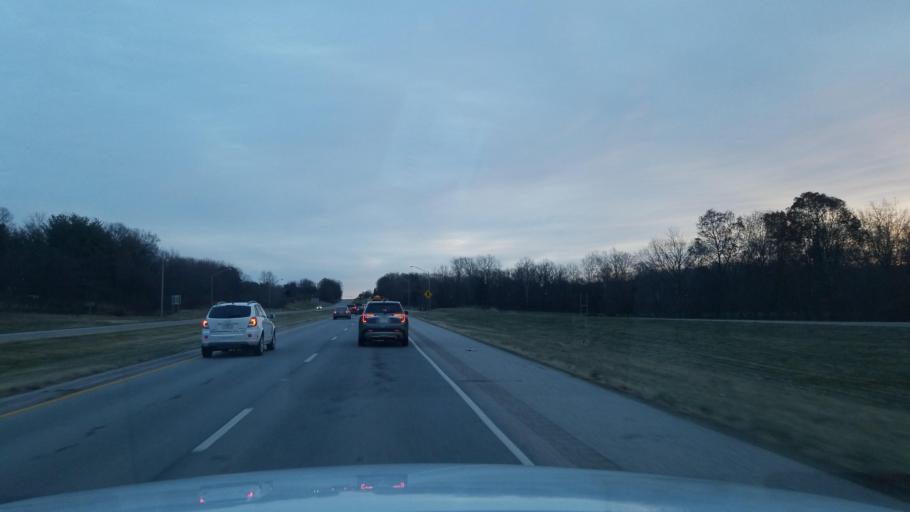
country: US
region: Indiana
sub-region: Vanderburgh County
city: Evansville
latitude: 37.9672
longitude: -87.6753
